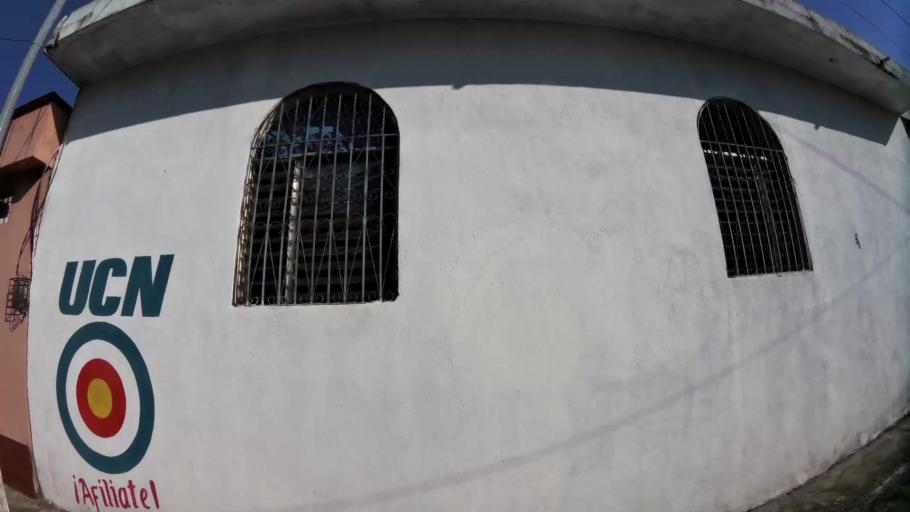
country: GT
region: Suchitepeque
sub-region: Municipio de San Gabriel
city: San Gabriel
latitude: 14.5294
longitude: -91.5155
